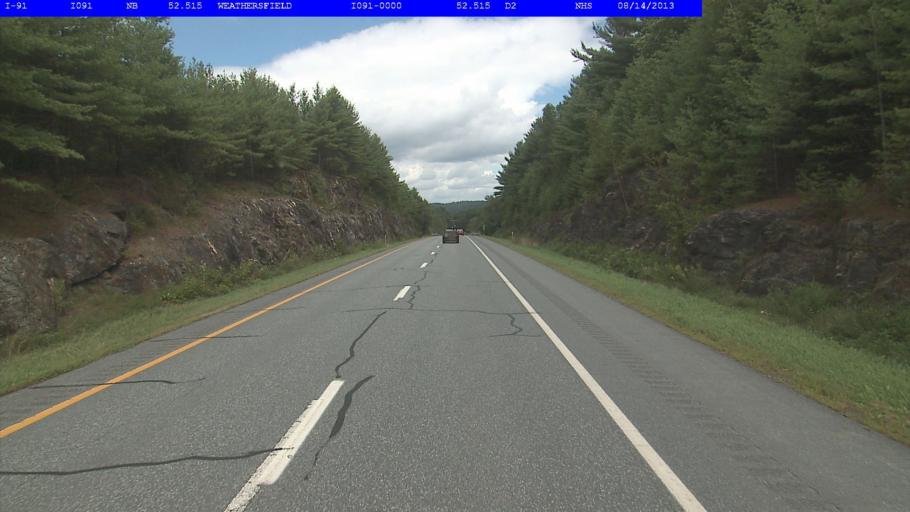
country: US
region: Vermont
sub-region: Windsor County
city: Windsor
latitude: 43.4188
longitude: -72.4122
